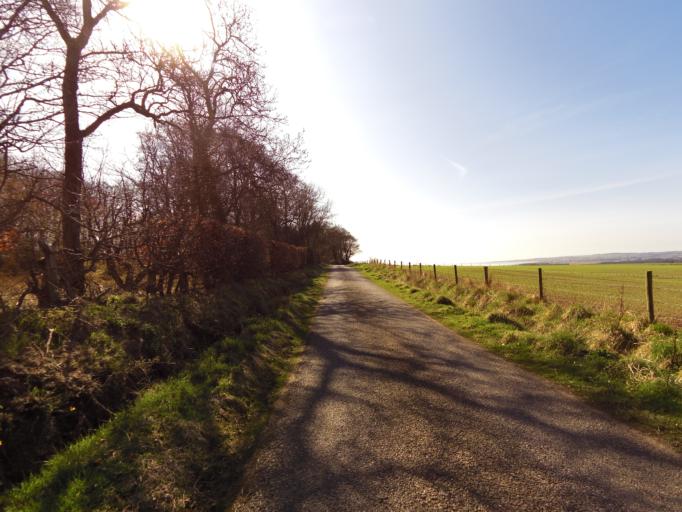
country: GB
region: Scotland
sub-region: Angus
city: Montrose
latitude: 56.7671
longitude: -2.4329
